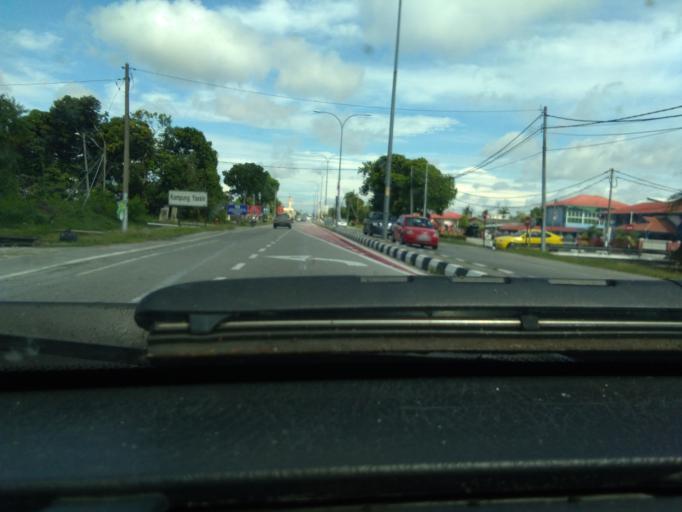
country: MY
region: Perak
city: Bagan Serai
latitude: 5.0071
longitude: 100.5417
